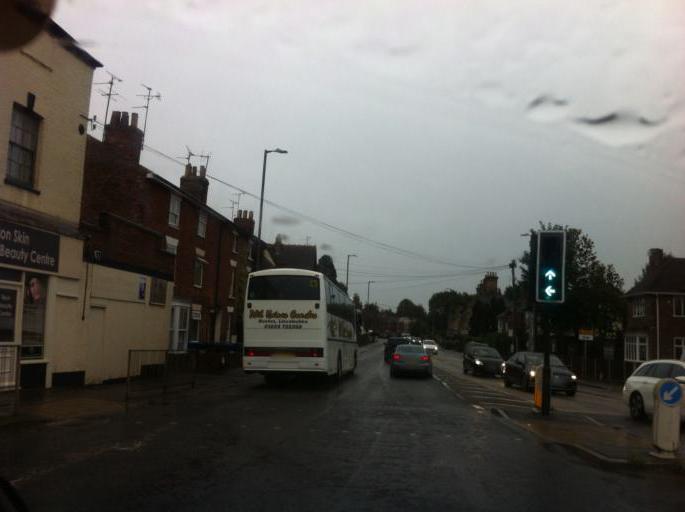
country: GB
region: England
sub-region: Lincolnshire
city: Boston
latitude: 52.9822
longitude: -0.0174
